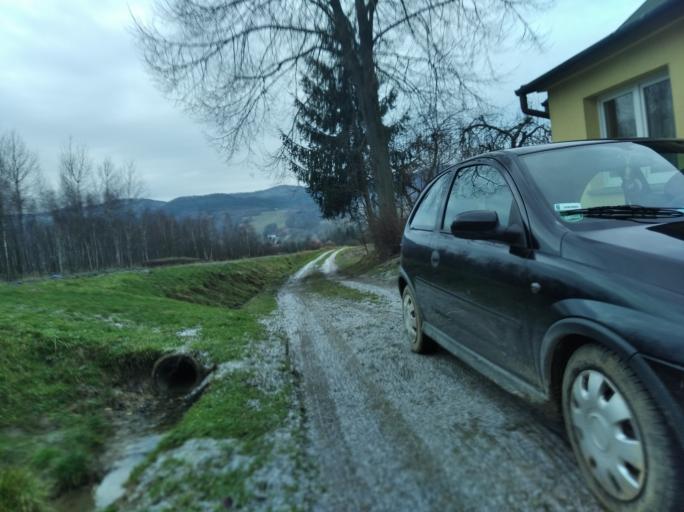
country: PL
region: Subcarpathian Voivodeship
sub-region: Powiat strzyzowski
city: Wysoka Strzyzowska
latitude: 49.8311
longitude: 21.7503
